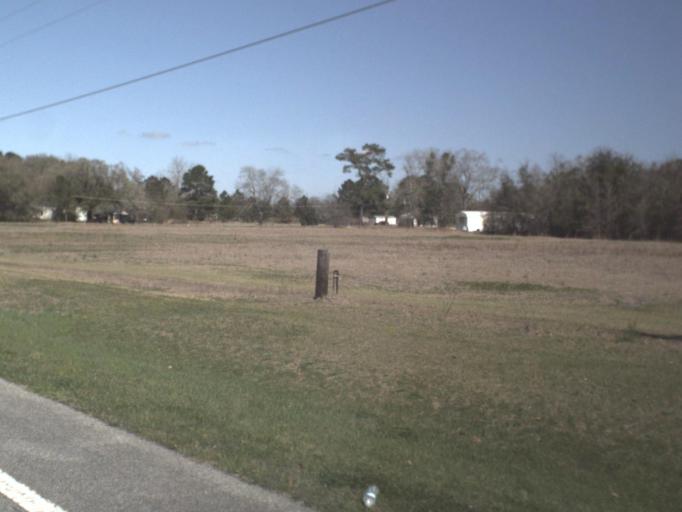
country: US
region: Florida
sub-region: Gadsden County
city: Gretna
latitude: 30.6914
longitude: -84.6224
